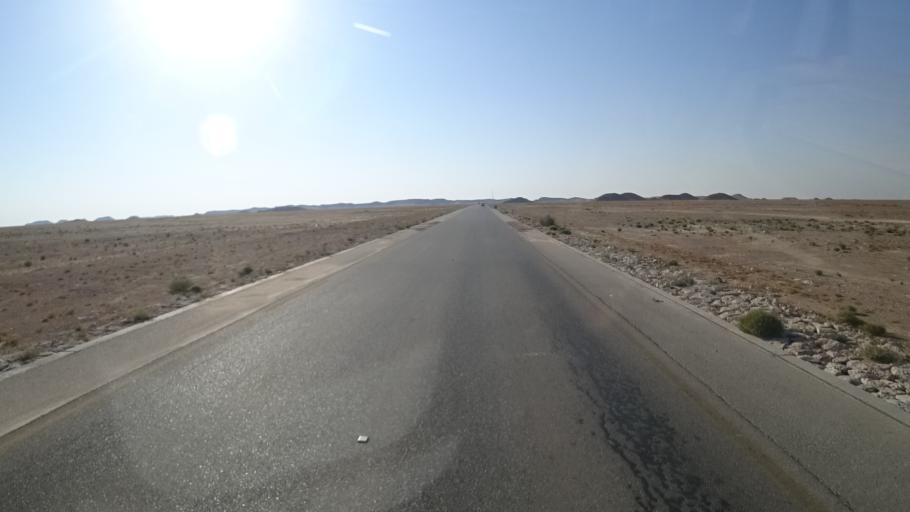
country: OM
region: Zufar
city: Salalah
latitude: 17.6391
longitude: 53.8811
